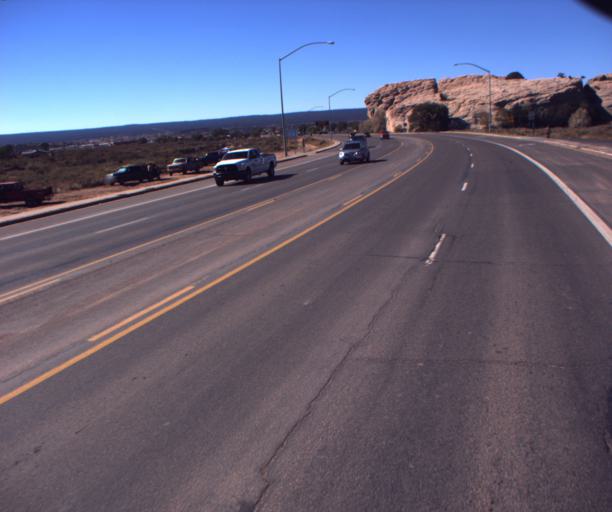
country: US
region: Arizona
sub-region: Apache County
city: Window Rock
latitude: 35.6626
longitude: -109.0468
